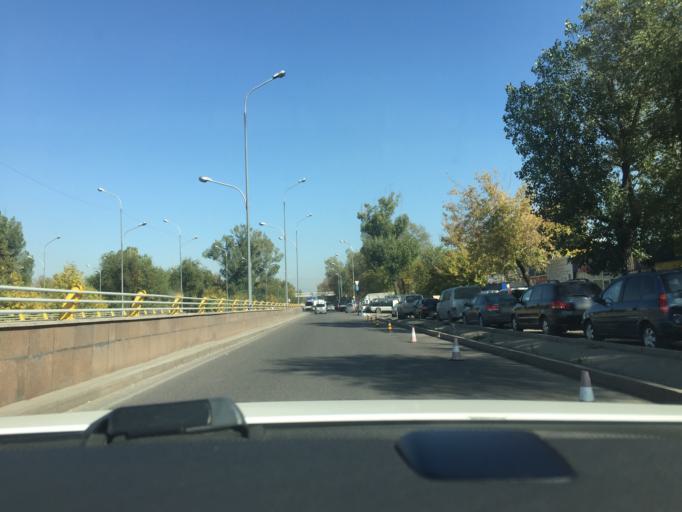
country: KZ
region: Almaty Qalasy
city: Almaty
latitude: 43.2591
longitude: 76.8881
